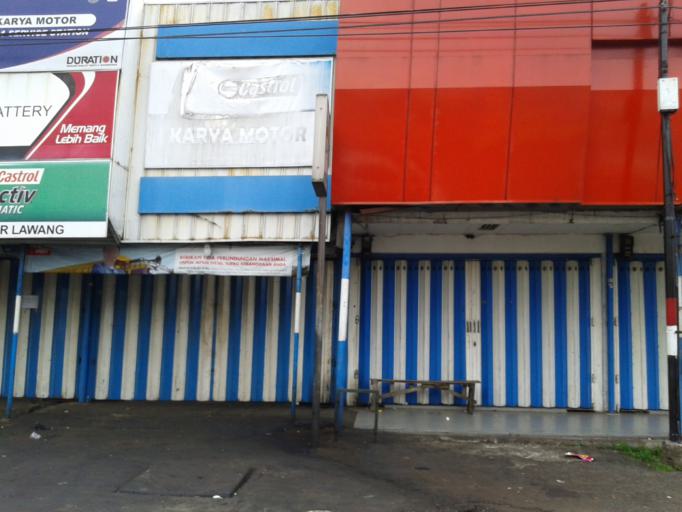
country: ID
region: East Java
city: Lawang
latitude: -7.8292
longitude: 112.7006
